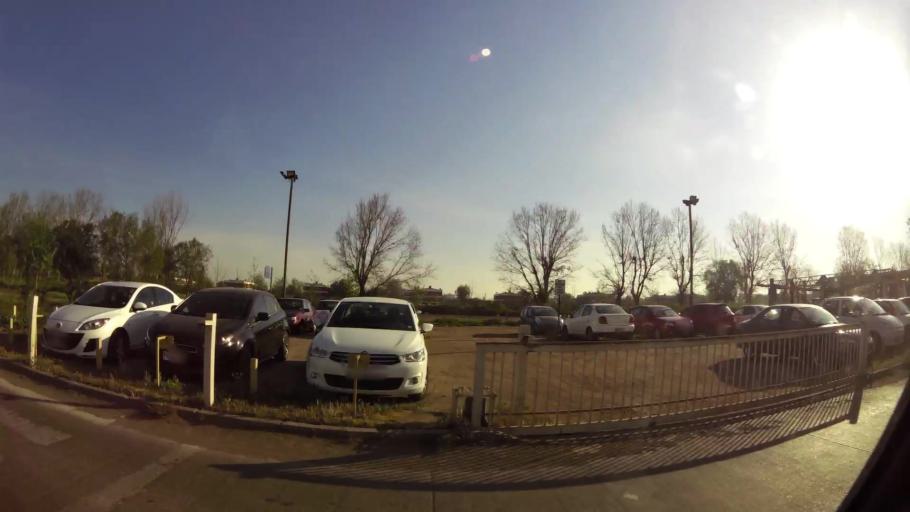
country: CL
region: Santiago Metropolitan
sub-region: Provincia de Santiago
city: Lo Prado
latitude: -33.4517
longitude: -70.7527
